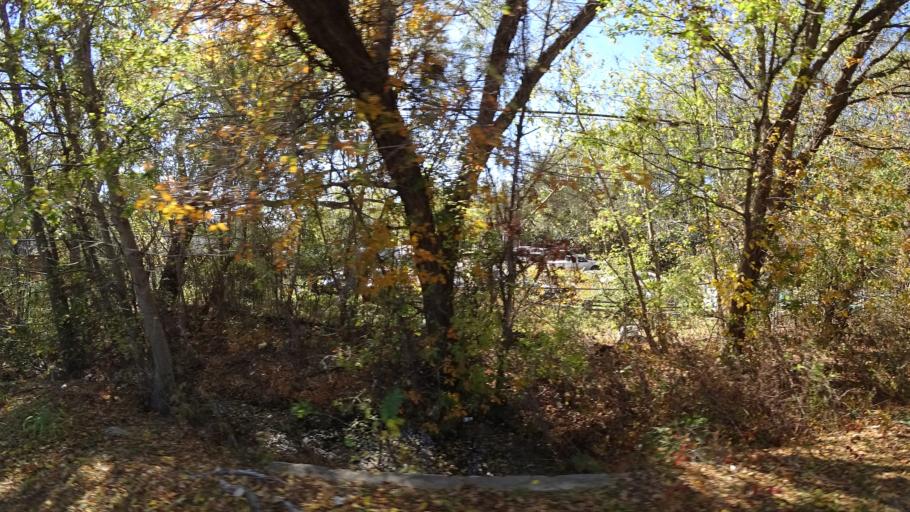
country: US
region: Texas
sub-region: Travis County
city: Wells Branch
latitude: 30.4349
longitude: -97.6867
